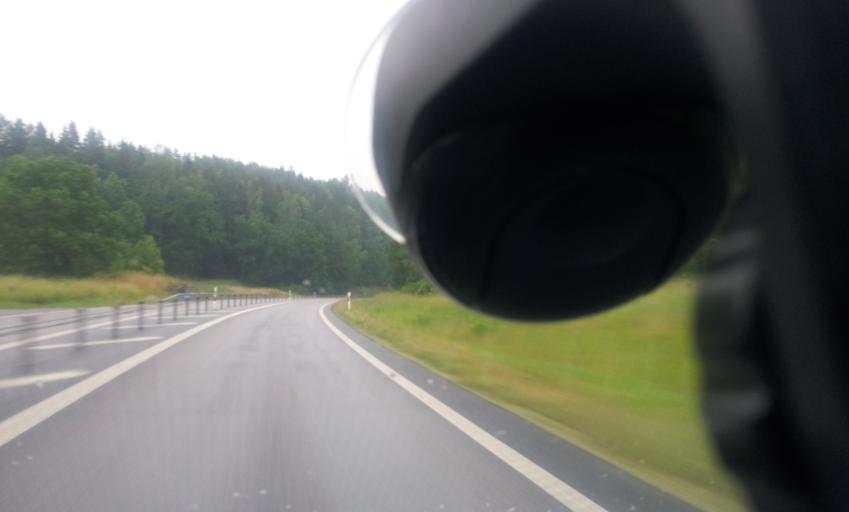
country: SE
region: Kalmar
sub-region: Vasterviks Kommun
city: Gamleby
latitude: 57.9293
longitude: 16.3983
